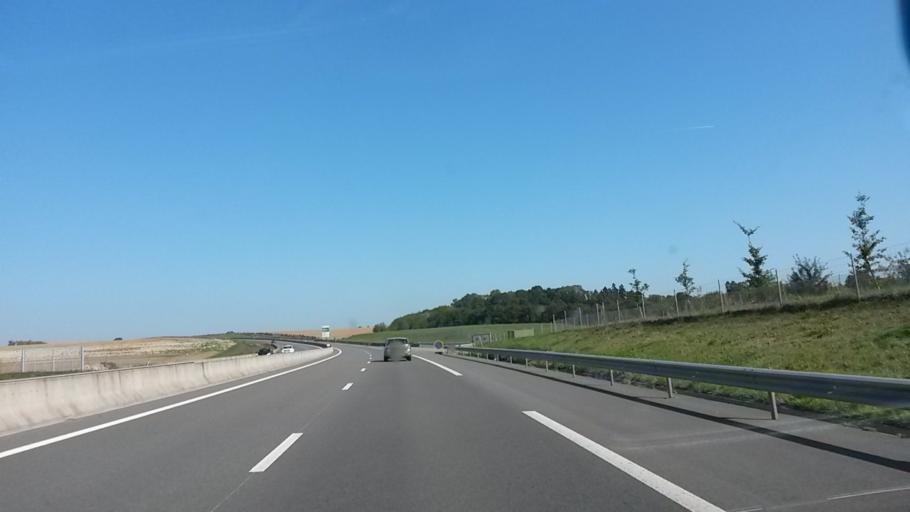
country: FR
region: Nord-Pas-de-Calais
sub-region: Departement du Nord
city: Louvroil
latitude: 50.2315
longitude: 3.9622
